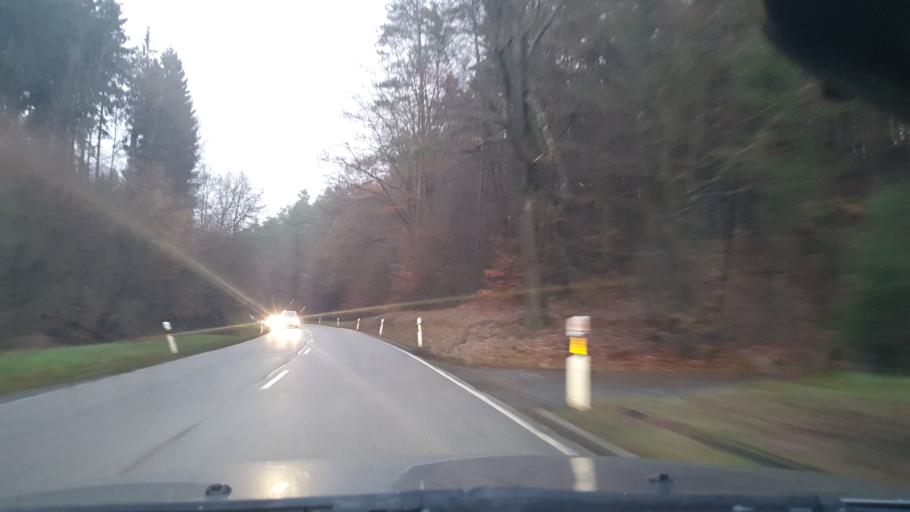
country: DE
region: Rheinland-Pfalz
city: Stelzenberg
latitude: 49.4197
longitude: 7.7330
